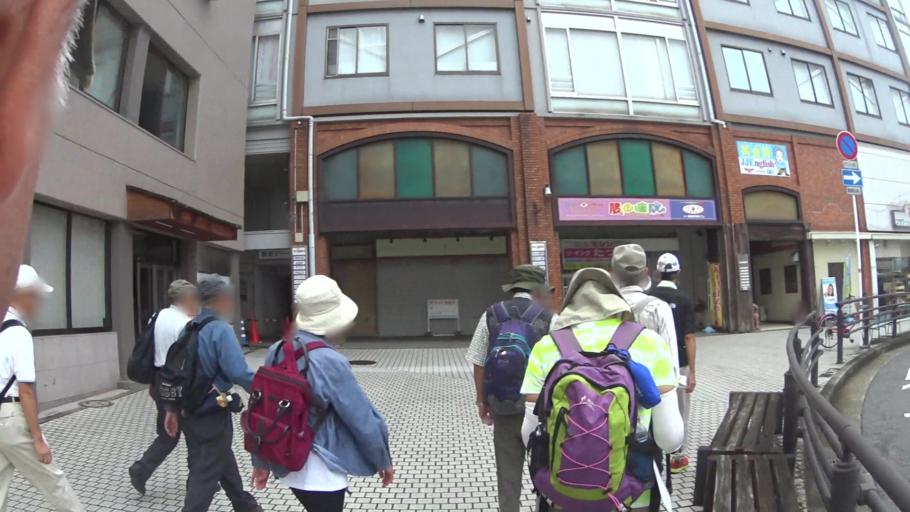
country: JP
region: Nara
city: Sakurai
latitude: 34.5121
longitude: 135.8470
